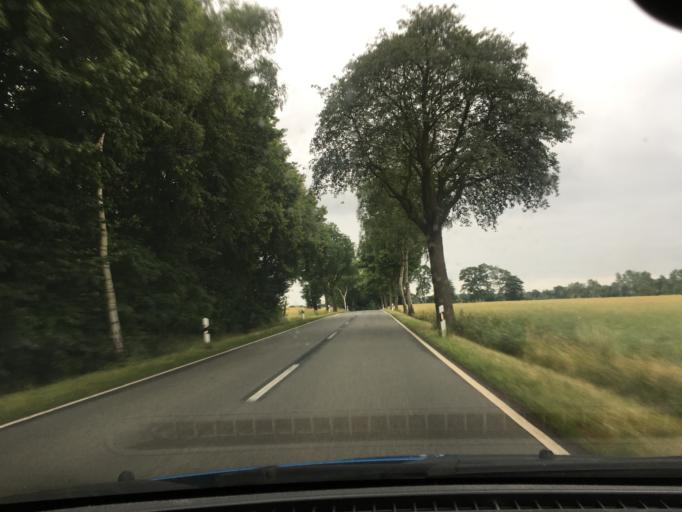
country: DE
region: Lower Saxony
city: Egestorf
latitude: 53.2036
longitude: 10.0683
